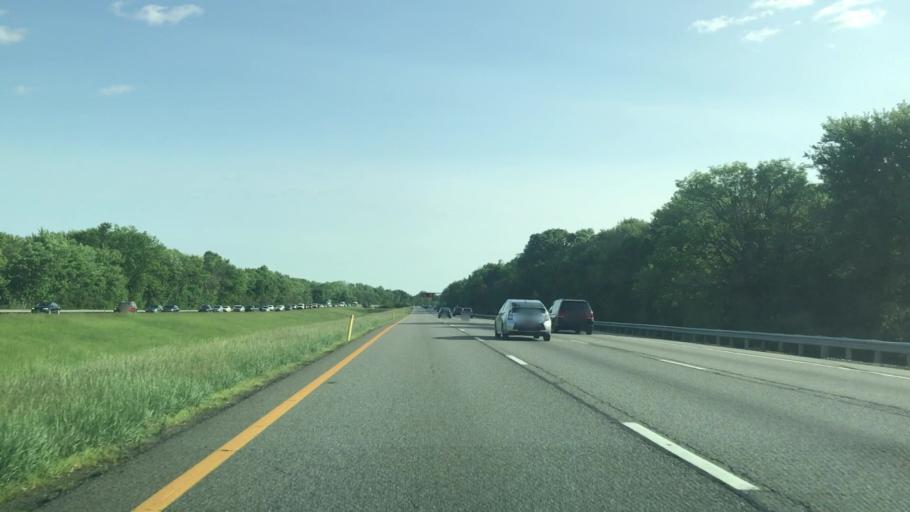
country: US
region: New Jersey
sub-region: Essex County
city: Fairfield
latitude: 40.8733
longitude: -74.3293
